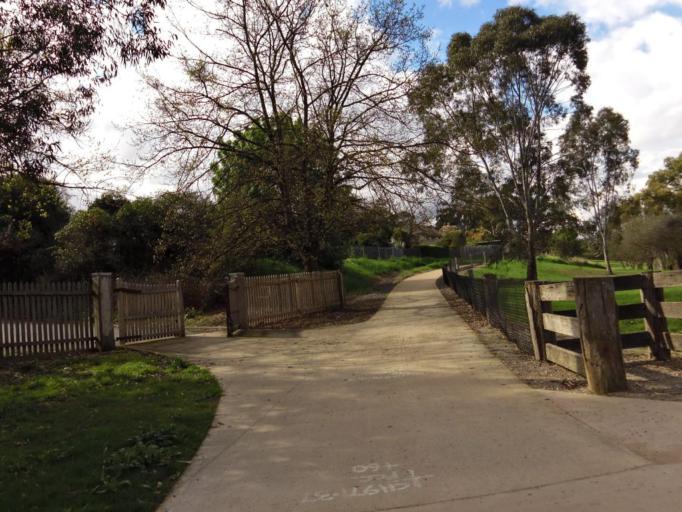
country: AU
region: Victoria
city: Rosanna
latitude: -37.7508
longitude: 145.0821
